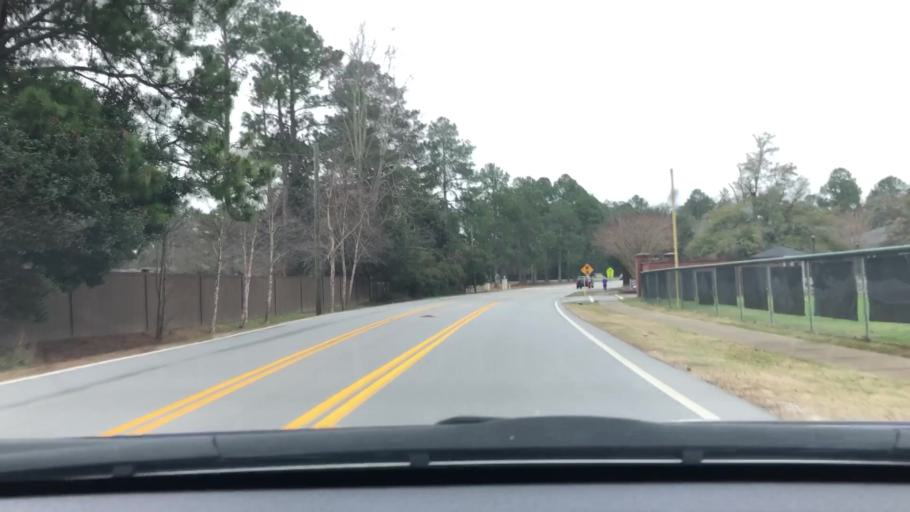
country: US
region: South Carolina
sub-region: Sumter County
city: Cherryvale
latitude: 33.9366
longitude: -80.4043
